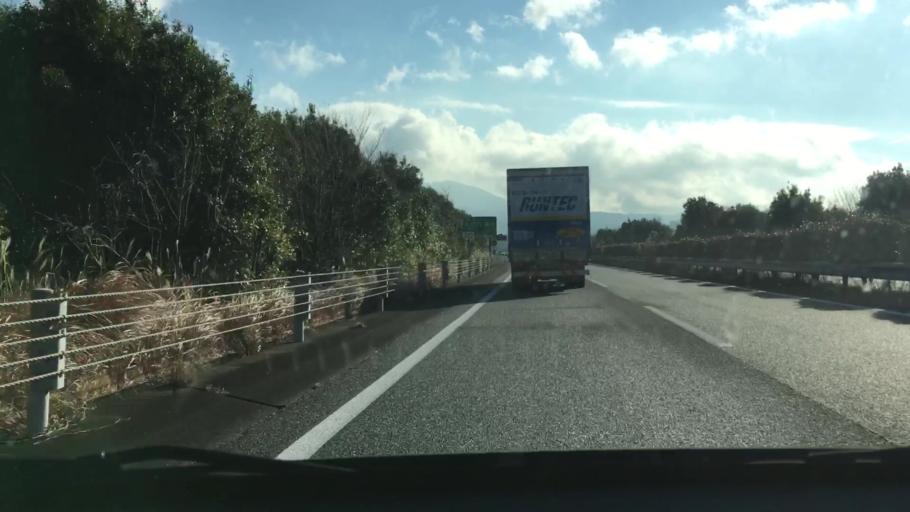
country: JP
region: Kumamoto
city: Hitoyoshi
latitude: 32.0582
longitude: 130.8030
